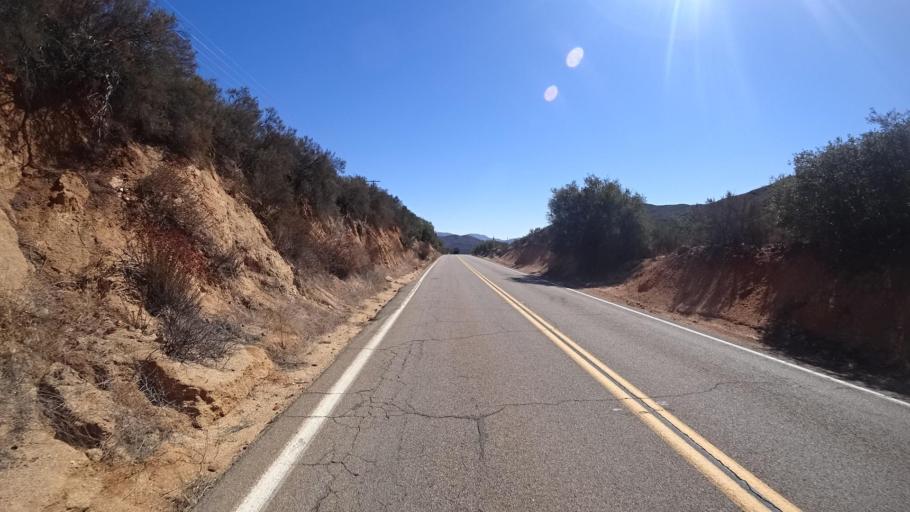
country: US
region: California
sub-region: San Diego County
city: Alpine
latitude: 32.7050
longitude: -116.7278
